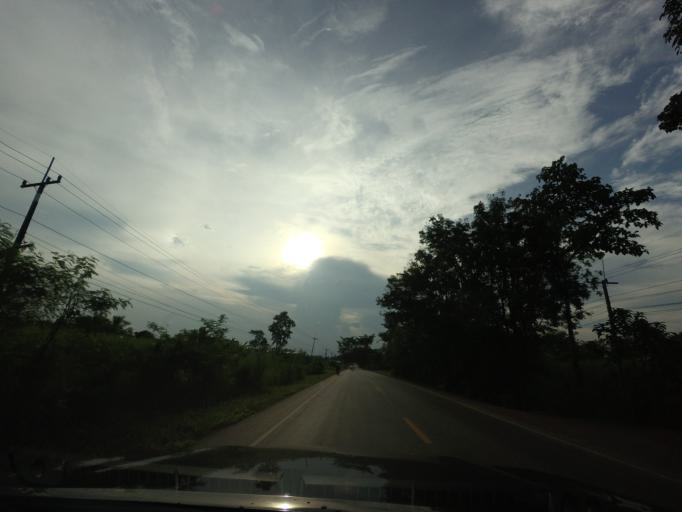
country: TH
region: Nong Khai
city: Pho Tak
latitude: 17.8038
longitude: 102.3078
